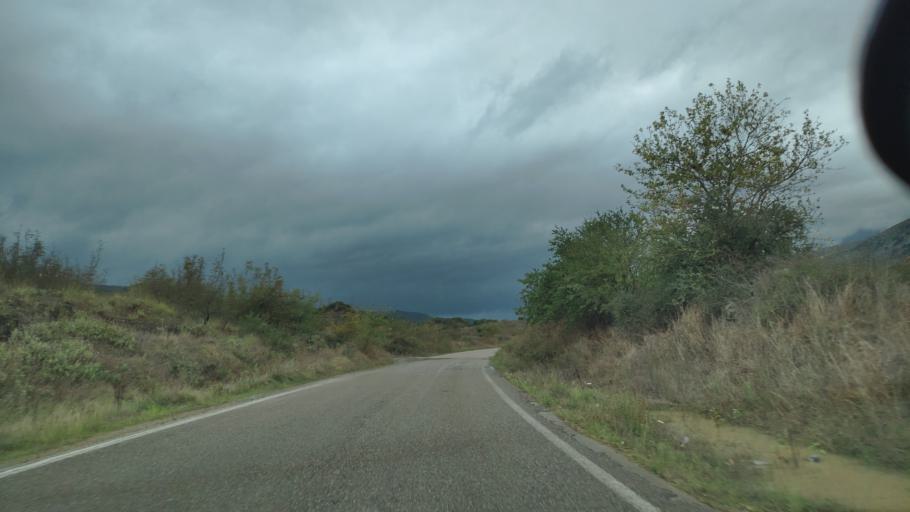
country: GR
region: West Greece
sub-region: Nomos Aitolias kai Akarnanias
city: Krikellos
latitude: 38.9793
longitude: 21.3237
